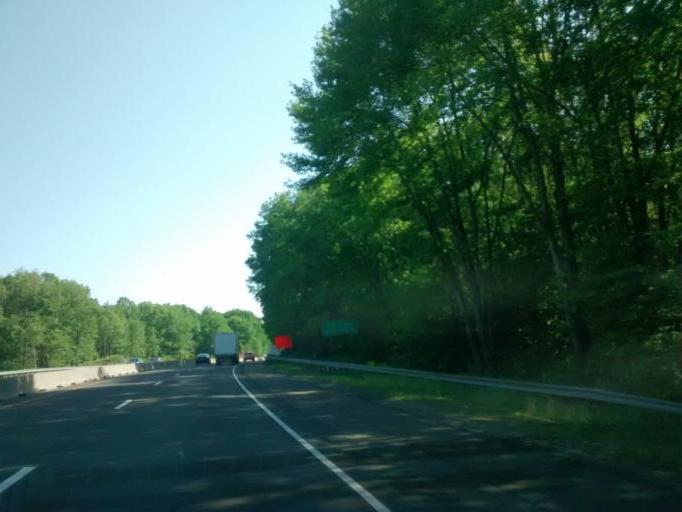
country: US
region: Connecticut
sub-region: New London County
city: Niantic
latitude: 41.3286
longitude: -72.2462
